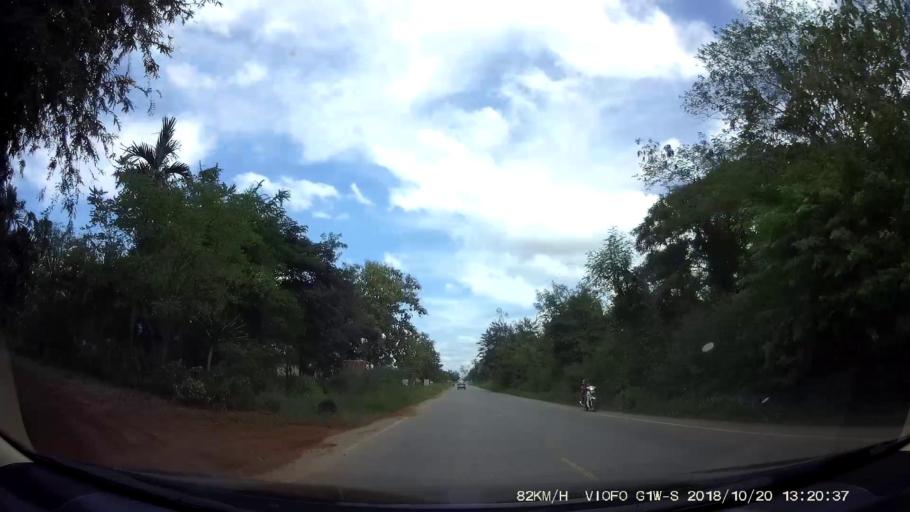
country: TH
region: Chaiyaphum
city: Khon San
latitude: 16.5502
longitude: 101.9052
